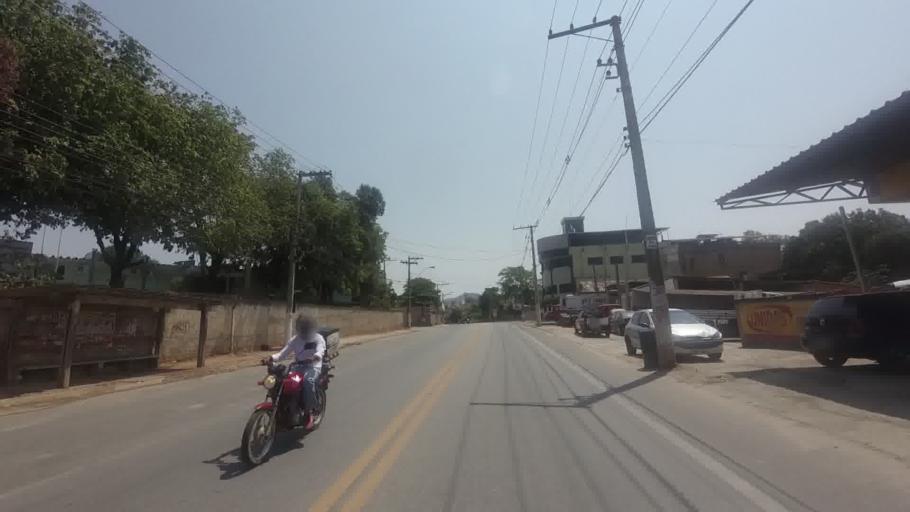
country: BR
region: Espirito Santo
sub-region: Cachoeiro De Itapemirim
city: Cachoeiro de Itapemirim
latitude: -20.8402
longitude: -41.1606
